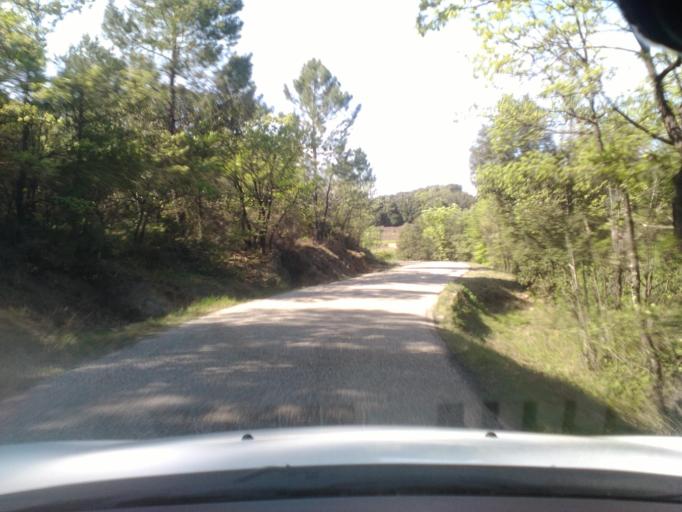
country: FR
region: Languedoc-Roussillon
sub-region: Departement du Gard
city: Lasalle
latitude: 44.0143
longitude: 3.8779
